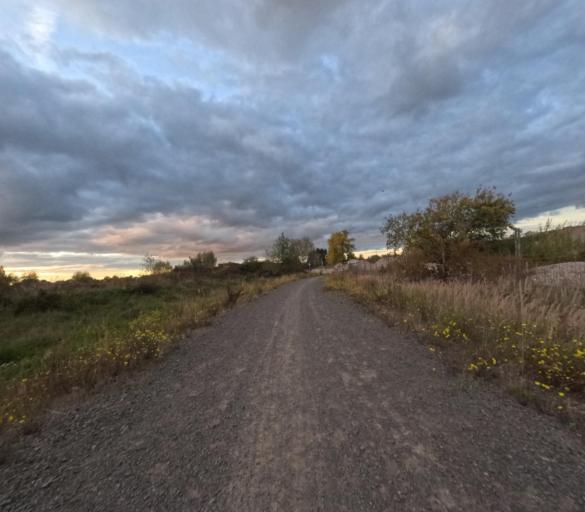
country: DE
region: Saxony
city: Borsdorf
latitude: 51.3069
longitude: 12.5316
